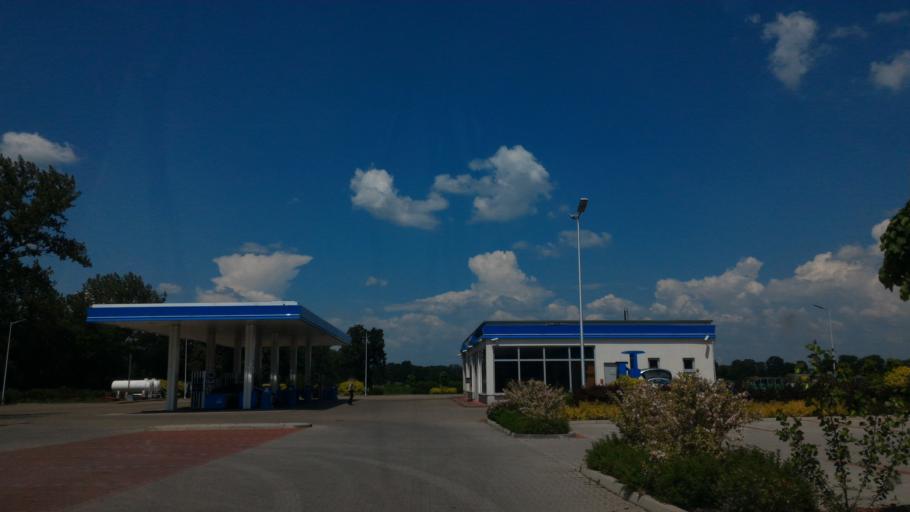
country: DE
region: Saxony
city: Zittau
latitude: 50.8762
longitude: 14.8261
